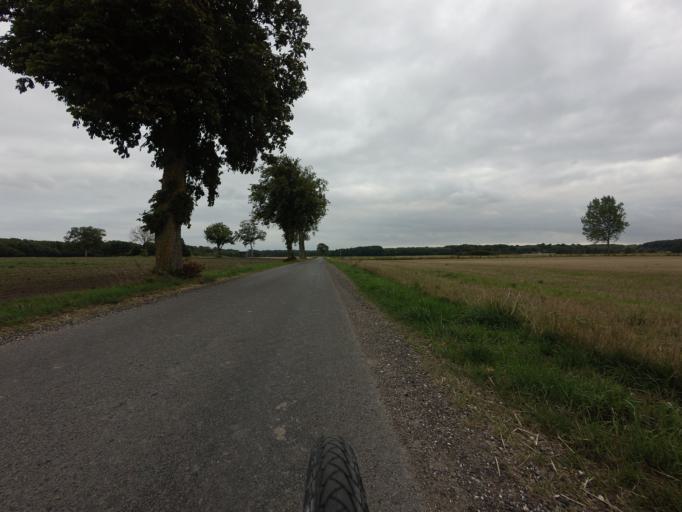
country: DK
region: Zealand
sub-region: Stevns Kommune
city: Store Heddinge
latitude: 55.3267
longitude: 12.3319
